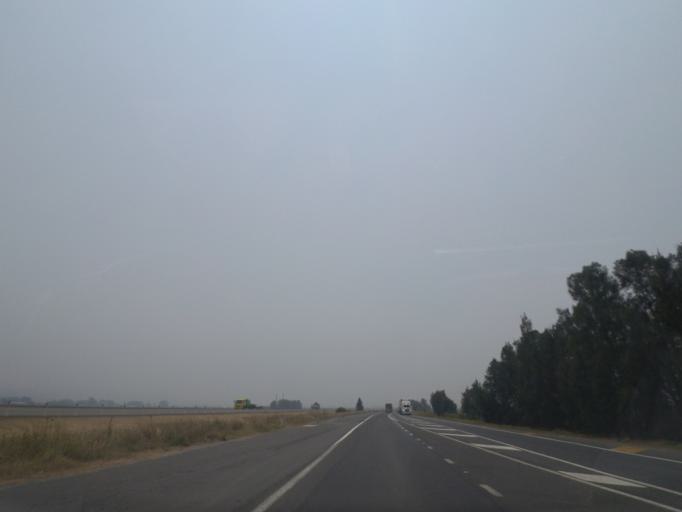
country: AU
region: New South Wales
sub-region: Clarence Valley
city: Maclean
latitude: -29.3910
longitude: 153.2400
